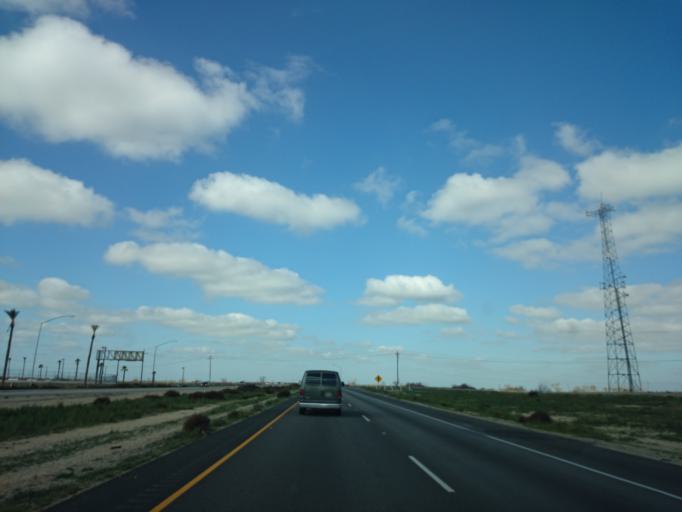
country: US
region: California
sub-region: Kern County
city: Rosedale
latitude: 35.2948
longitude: -119.2538
